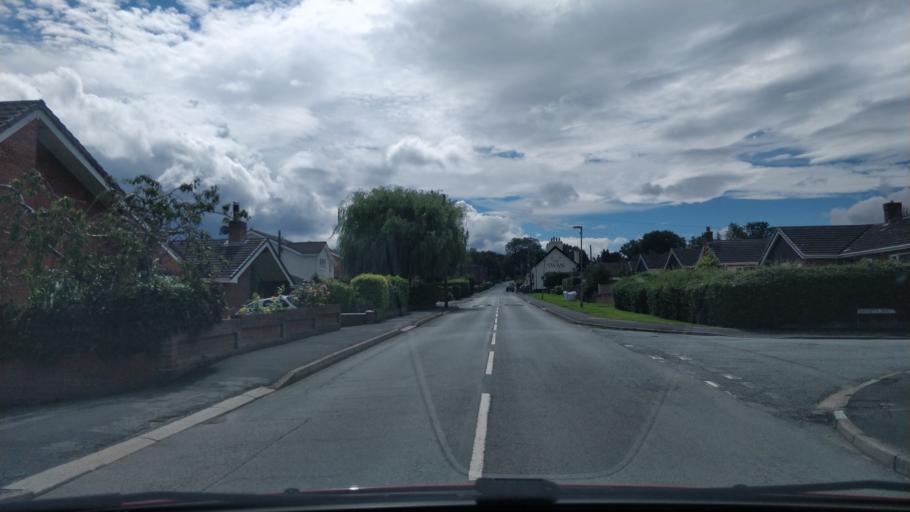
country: GB
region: Wales
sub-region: County of Flintshire
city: Hope
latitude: 53.1429
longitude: -3.0049
